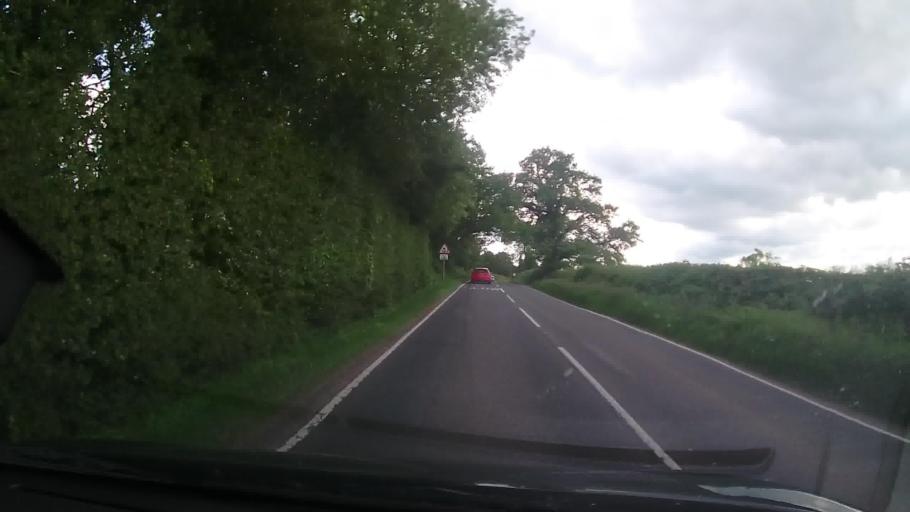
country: GB
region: England
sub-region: Shropshire
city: Clive
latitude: 52.8278
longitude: -2.7351
